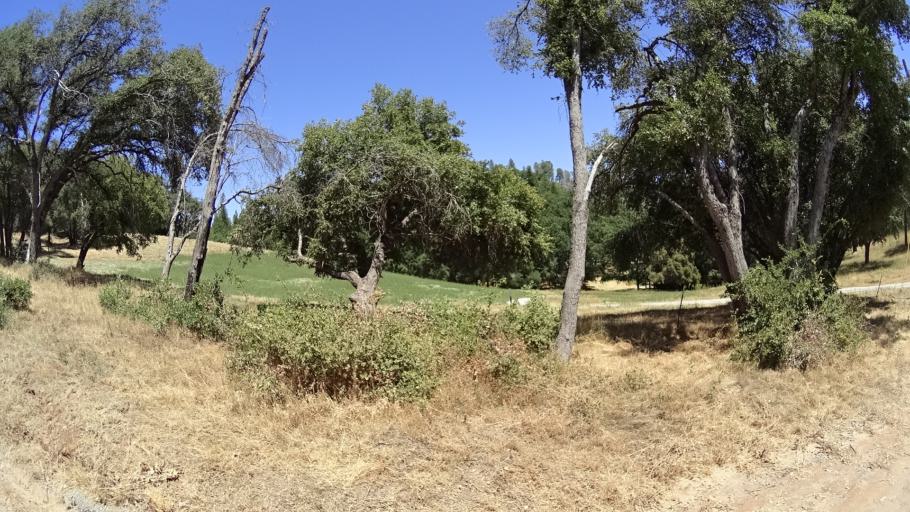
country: US
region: California
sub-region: Calaveras County
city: Mountain Ranch
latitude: 38.2845
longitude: -120.5980
